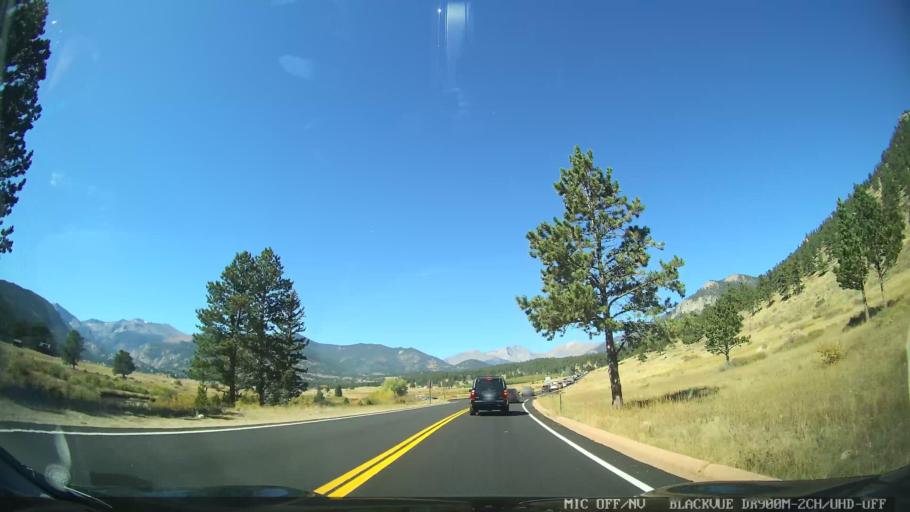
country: US
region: Colorado
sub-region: Larimer County
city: Estes Park
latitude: 40.3525
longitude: -105.5812
